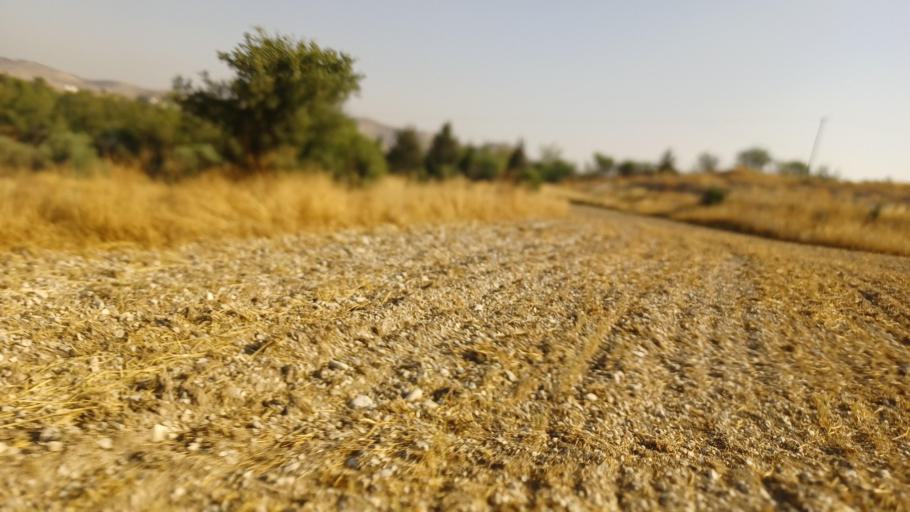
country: CY
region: Lefkosia
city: Lympia
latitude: 34.9885
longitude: 33.4600
